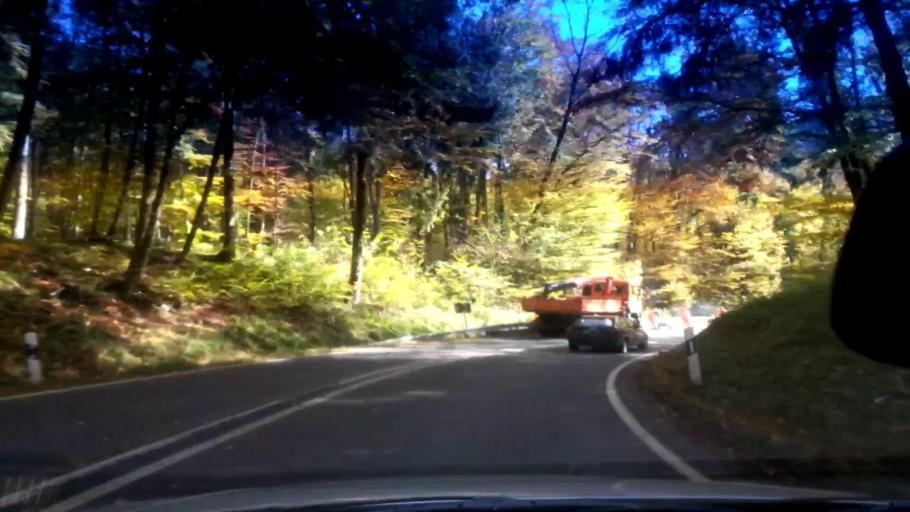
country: DE
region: Bavaria
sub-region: Upper Franconia
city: Poxdorf
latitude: 49.9783
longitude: 11.0983
